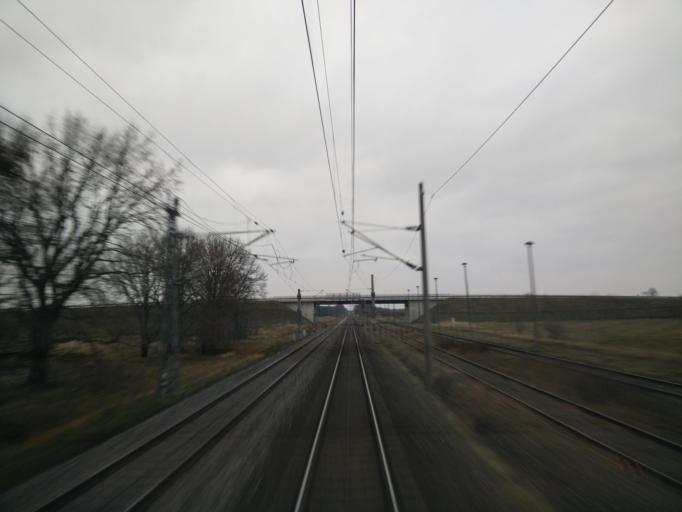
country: DE
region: Brandenburg
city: Karstadt
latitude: 53.1713
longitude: 11.7370
